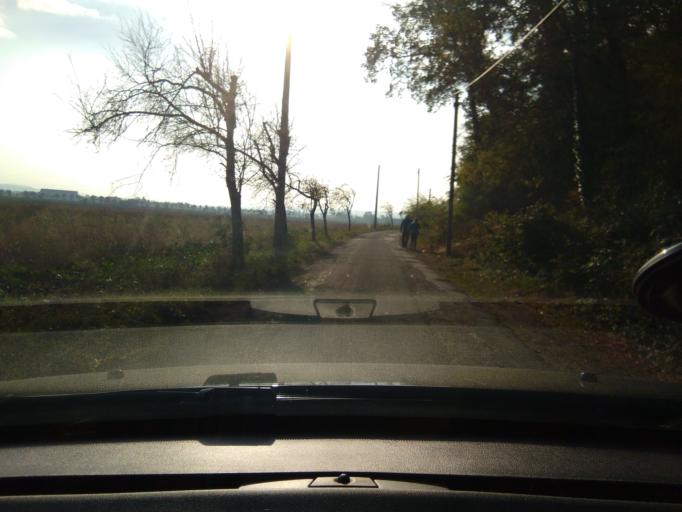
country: DE
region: Saxony
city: Niederau
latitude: 51.1484
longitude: 13.5200
